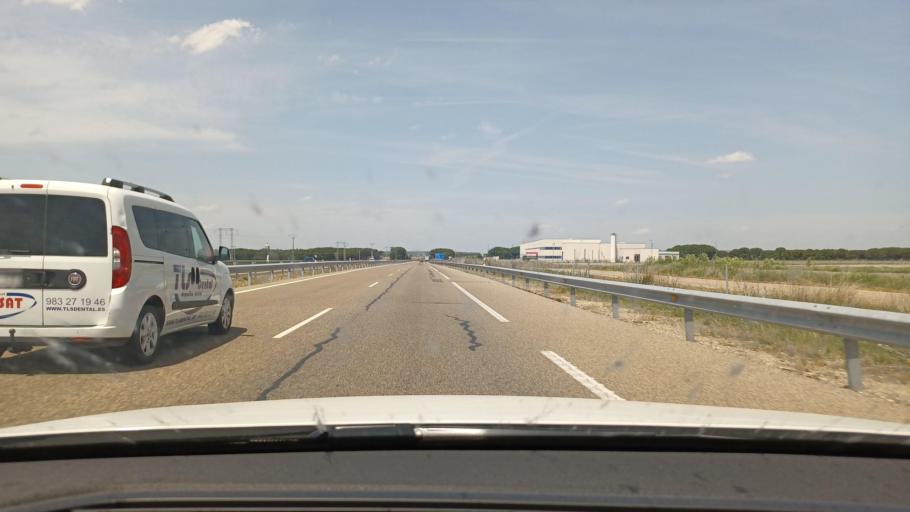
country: ES
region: Castille and Leon
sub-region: Provincia de Valladolid
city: Aldeamayor de San Martin
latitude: 41.5023
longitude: -4.6249
